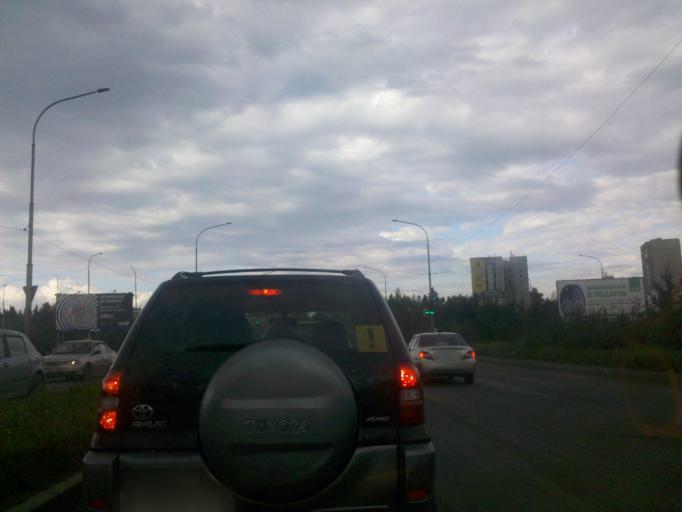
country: RU
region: Republic of Karelia
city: Petrozavodsk
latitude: 61.7940
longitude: 34.3004
